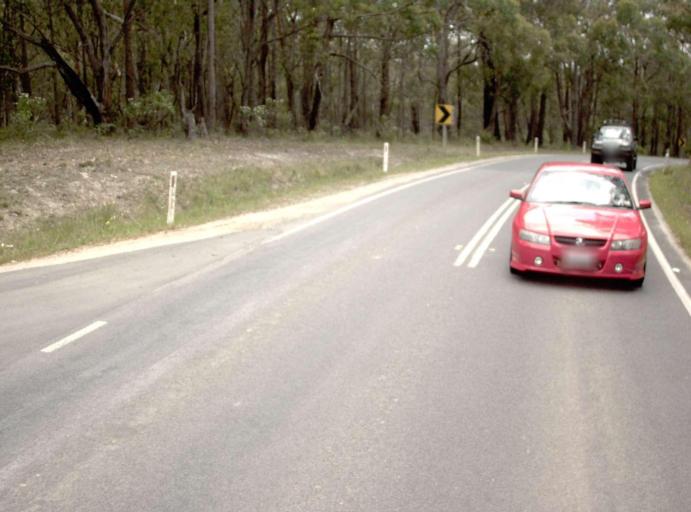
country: AU
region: Victoria
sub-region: Latrobe
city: Traralgon
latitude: -38.4179
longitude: 146.7474
